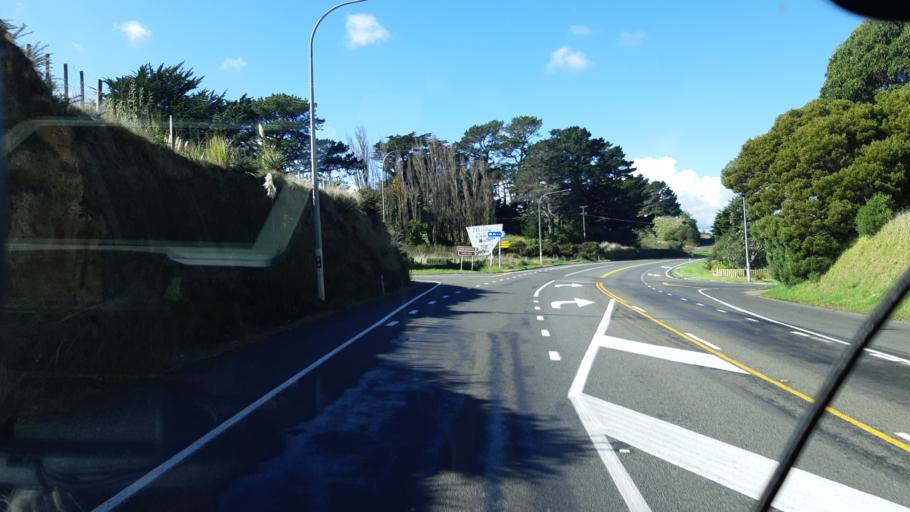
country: NZ
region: Manawatu-Wanganui
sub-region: Wanganui District
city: Wanganui
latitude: -39.9576
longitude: 175.0792
